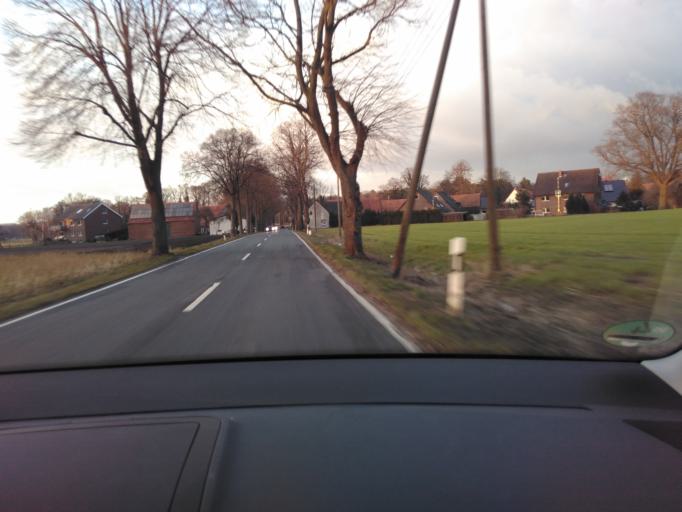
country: DE
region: North Rhine-Westphalia
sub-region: Regierungsbezirk Detmold
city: Verl
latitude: 51.9437
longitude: 8.4903
